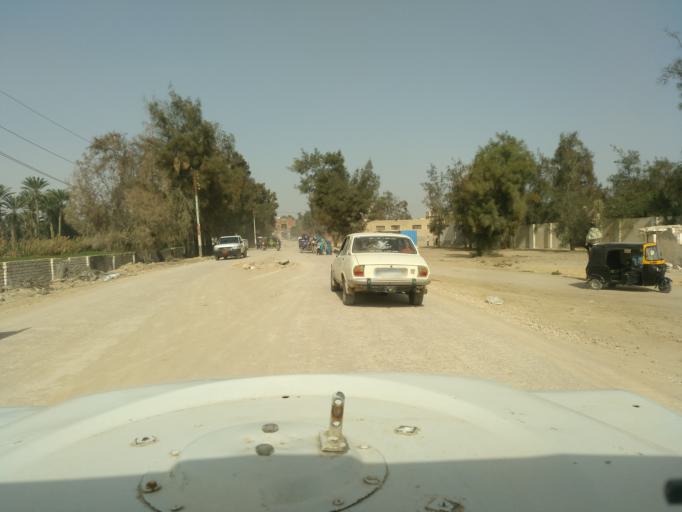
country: EG
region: Al Buhayrah
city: Beheira
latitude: 30.3690
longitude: 30.3580
